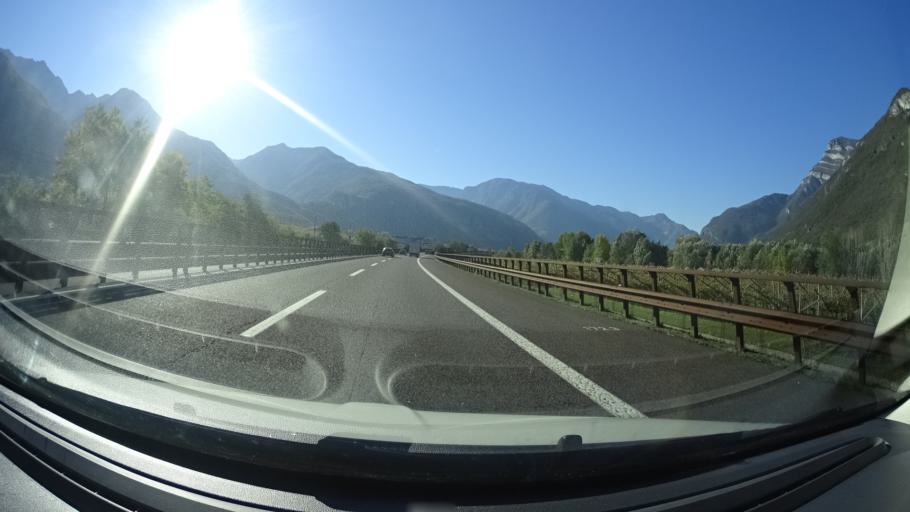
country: IT
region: Trentino-Alto Adige
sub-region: Provincia di Trento
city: Ala
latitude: 45.7974
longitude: 11.0204
